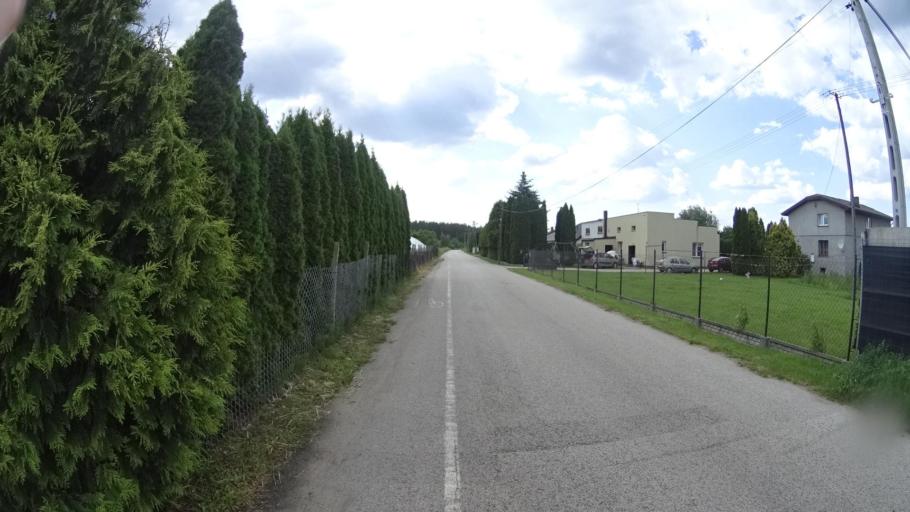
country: PL
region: Masovian Voivodeship
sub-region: Powiat piaseczynski
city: Tarczyn
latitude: 51.9966
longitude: 20.8400
